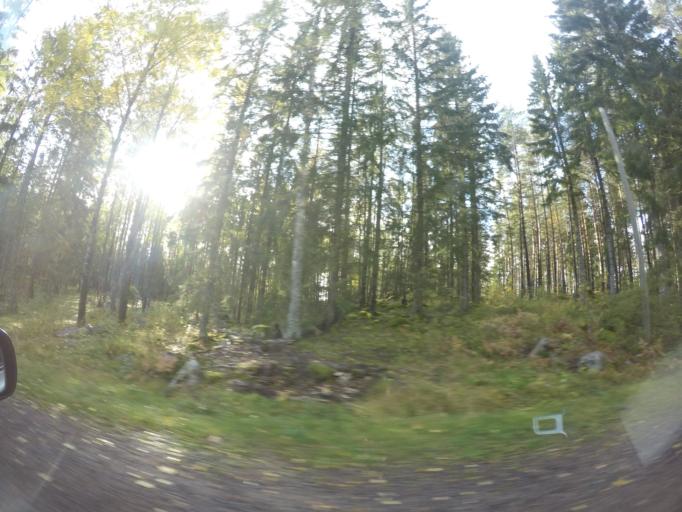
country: SE
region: Soedermanland
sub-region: Eskilstuna Kommun
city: Kvicksund
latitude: 59.3632
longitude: 16.2627
